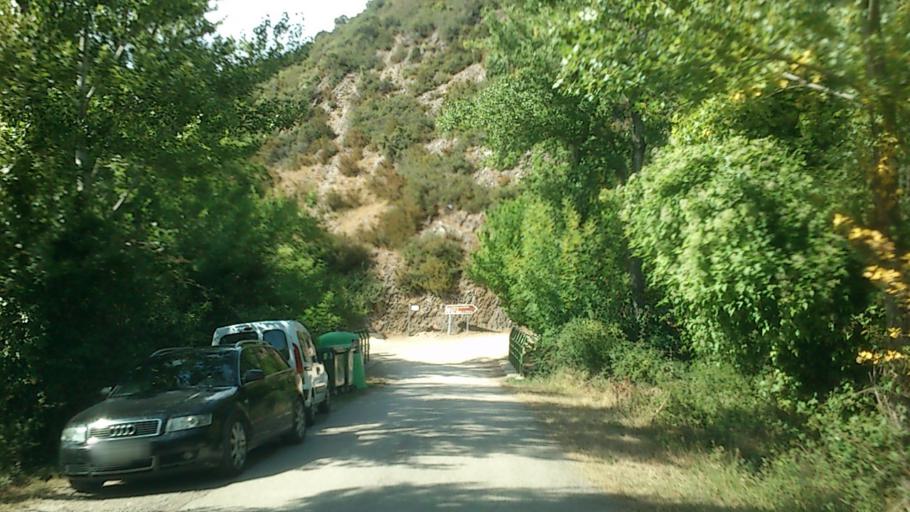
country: ES
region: Castille and Leon
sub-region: Provincia de Burgos
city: Frias
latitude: 42.8237
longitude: -3.2272
